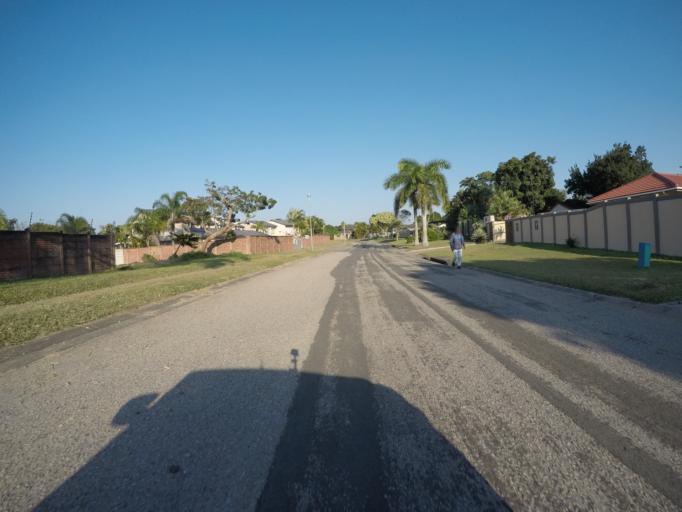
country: ZA
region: KwaZulu-Natal
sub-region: uThungulu District Municipality
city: Richards Bay
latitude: -28.7785
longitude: 32.1044
